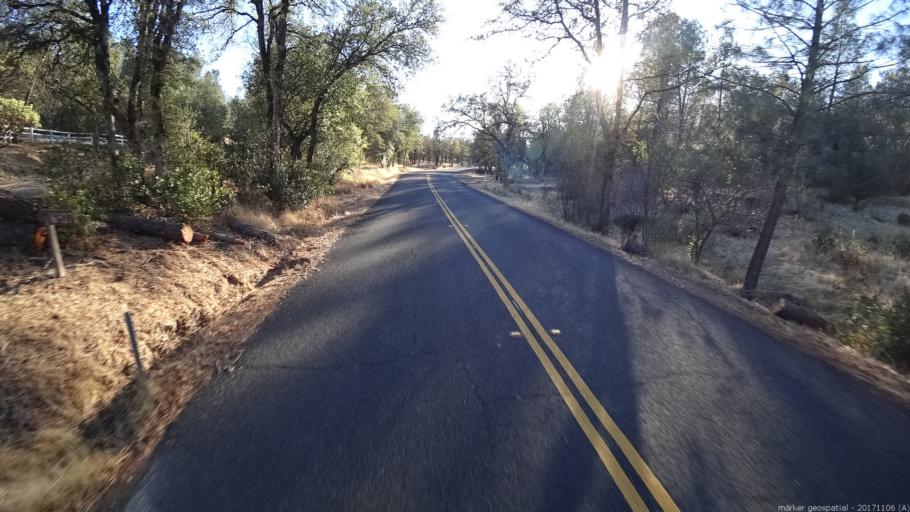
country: US
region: California
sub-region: Shasta County
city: Shasta
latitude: 40.5814
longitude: -122.4497
